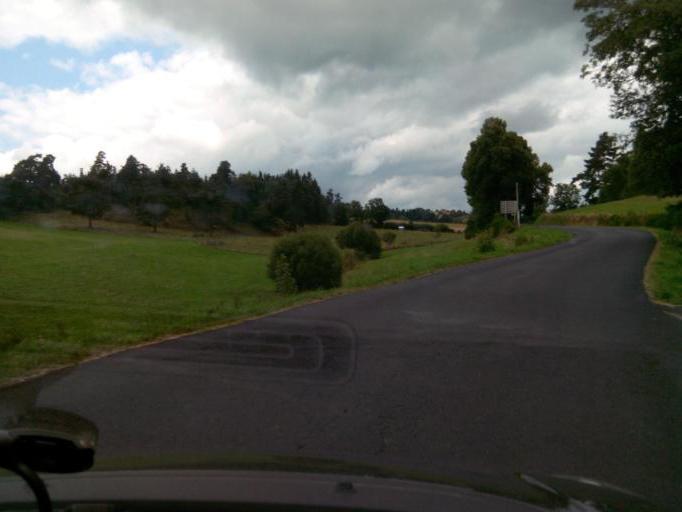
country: FR
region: Rhone-Alpes
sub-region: Departement de la Loire
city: Usson-en-Forez
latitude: 45.3617
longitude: 3.9591
